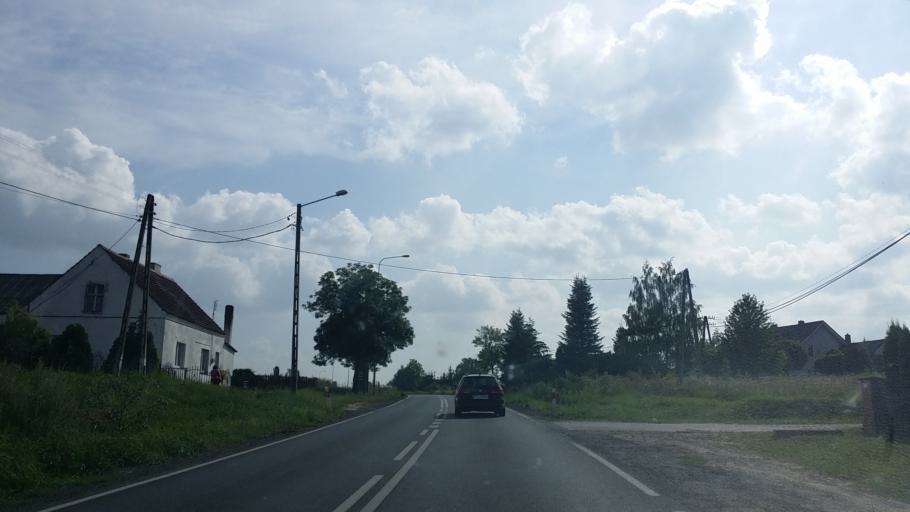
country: PL
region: West Pomeranian Voivodeship
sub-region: Powiat mysliborski
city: Barlinek
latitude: 52.9819
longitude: 15.1945
